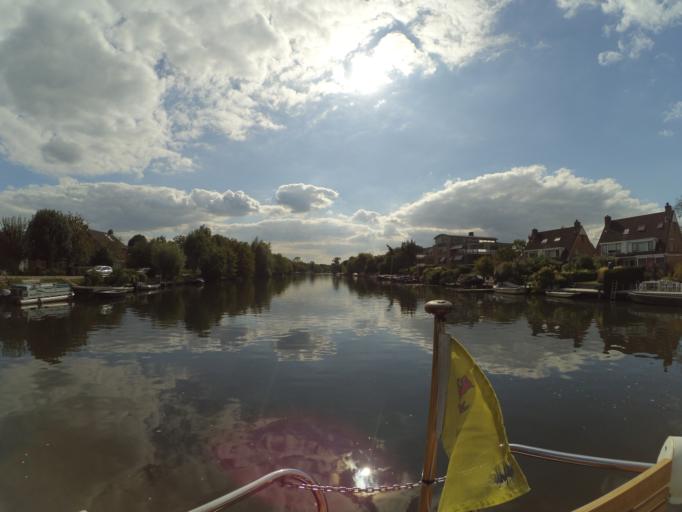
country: NL
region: Utrecht
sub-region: Stichtse Vecht
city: Breukelen
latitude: 52.1849
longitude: 5.0073
